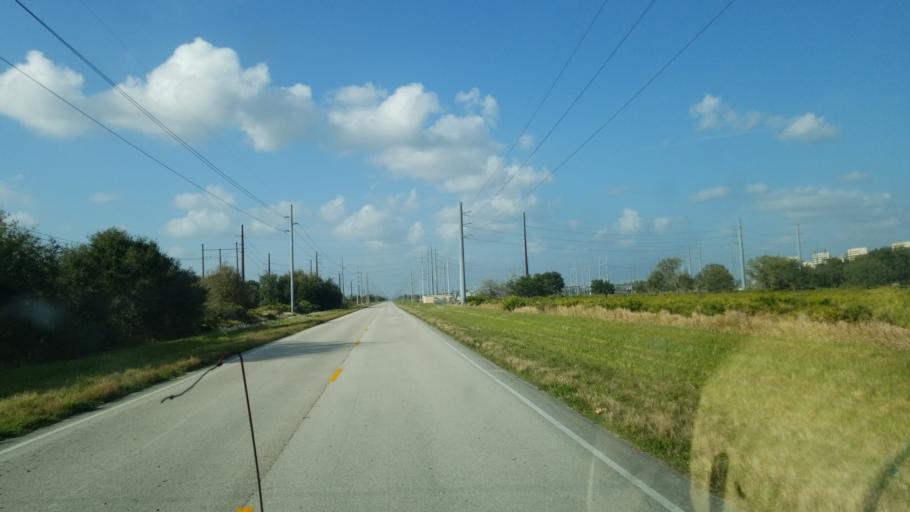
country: US
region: Florida
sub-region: Hardee County
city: Wauchula
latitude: 27.5199
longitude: -81.9261
